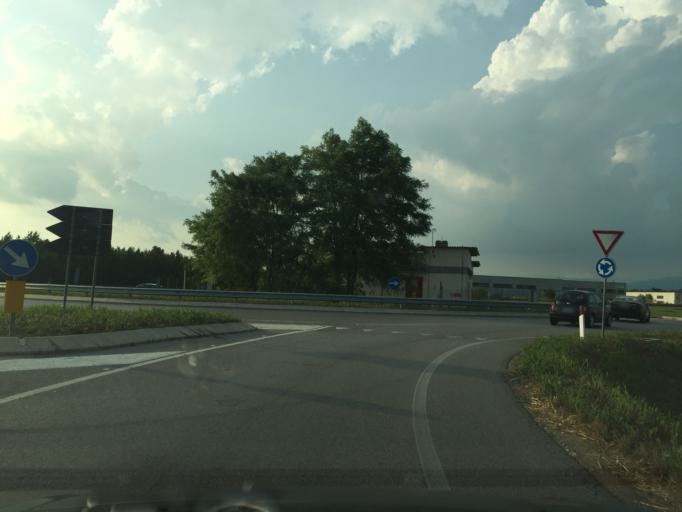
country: IT
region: Friuli Venezia Giulia
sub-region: Provincia di Udine
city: Manzano
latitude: 45.9785
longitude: 13.3543
